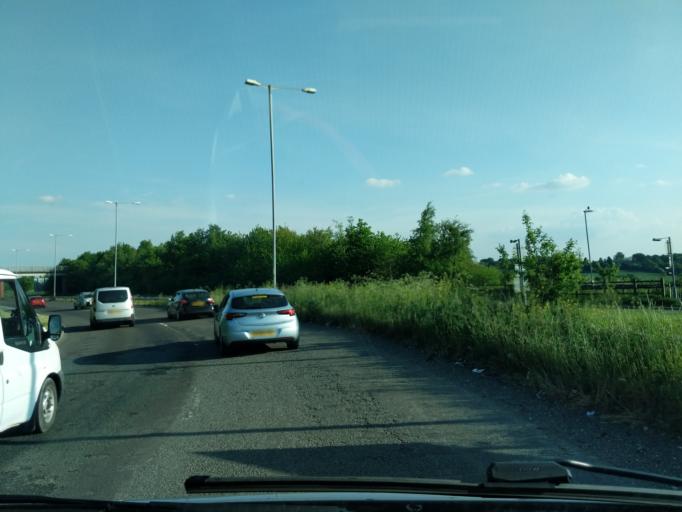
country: GB
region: England
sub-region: Borough of Halton
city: Widnes
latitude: 53.4022
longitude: -2.7453
